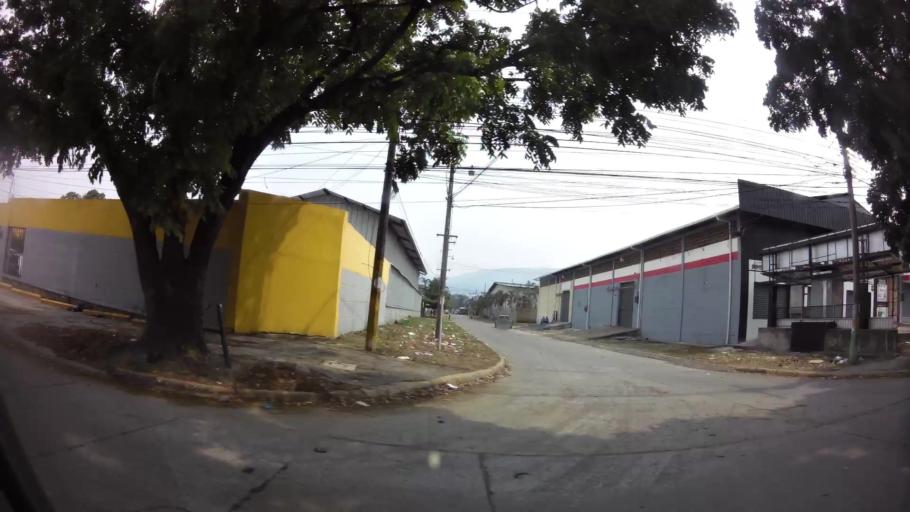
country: HN
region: Cortes
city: San Pedro Sula
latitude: 15.4900
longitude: -88.0225
